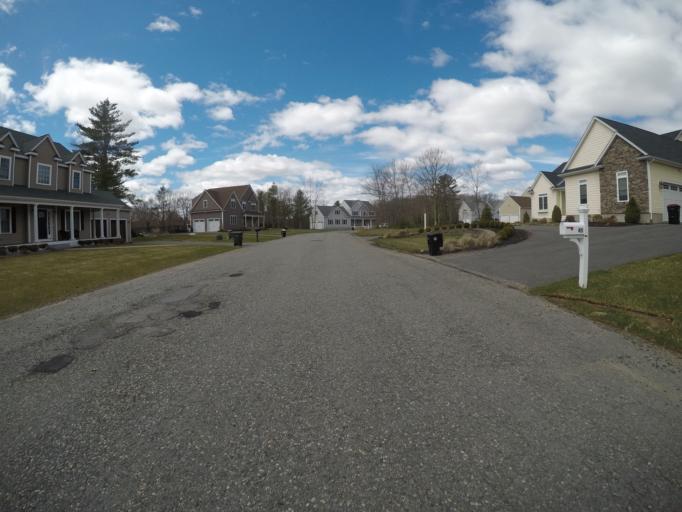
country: US
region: Massachusetts
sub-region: Norfolk County
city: Stoughton
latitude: 42.0786
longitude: -71.0747
